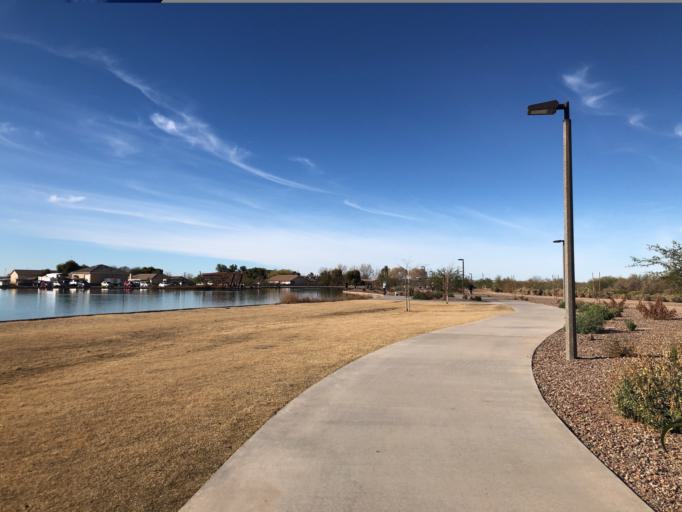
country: US
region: Arizona
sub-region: Maricopa County
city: Queen Creek
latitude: 33.2557
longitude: -111.6585
